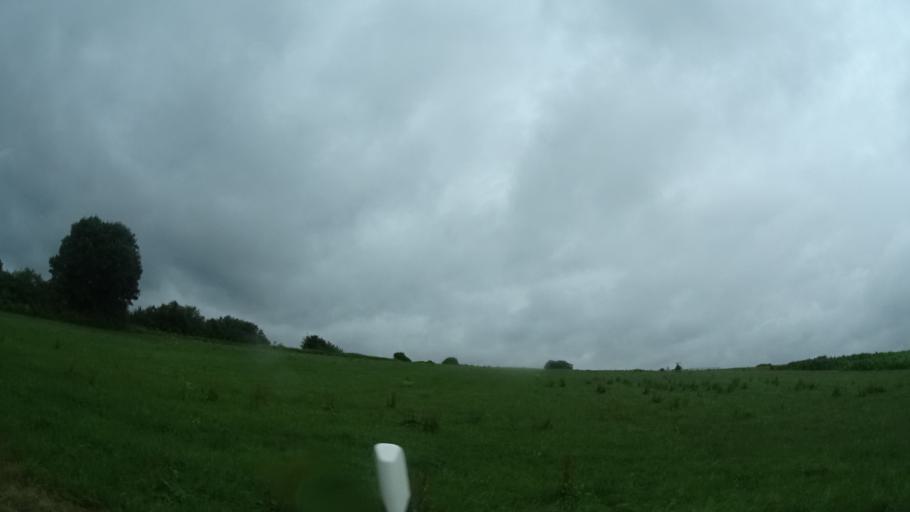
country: LU
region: Luxembourg
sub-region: Canton de Capellen
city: Clemency
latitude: 49.5946
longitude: 5.8514
